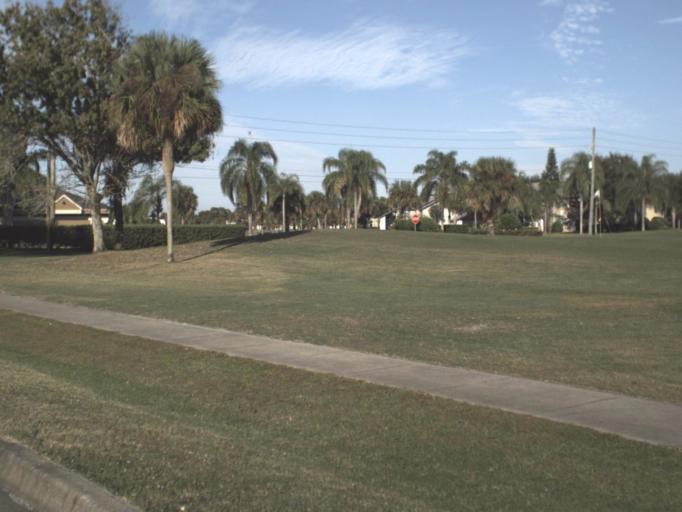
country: US
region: Florida
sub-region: Brevard County
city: June Park
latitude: 28.1486
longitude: -80.6718
